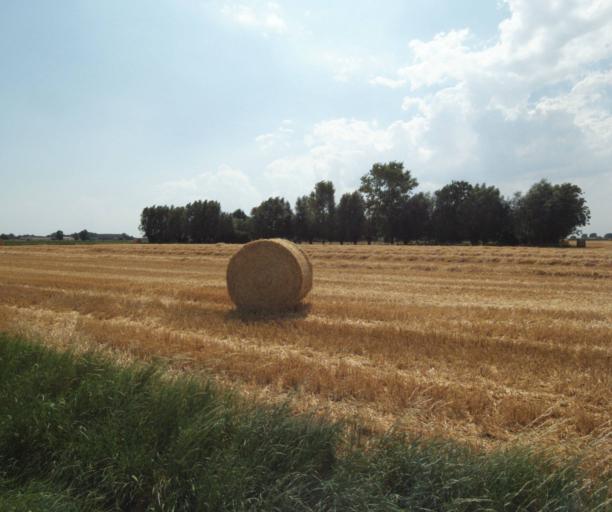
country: FR
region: Nord-Pas-de-Calais
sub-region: Departement du Nord
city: Comines
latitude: 50.7473
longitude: 3.0050
